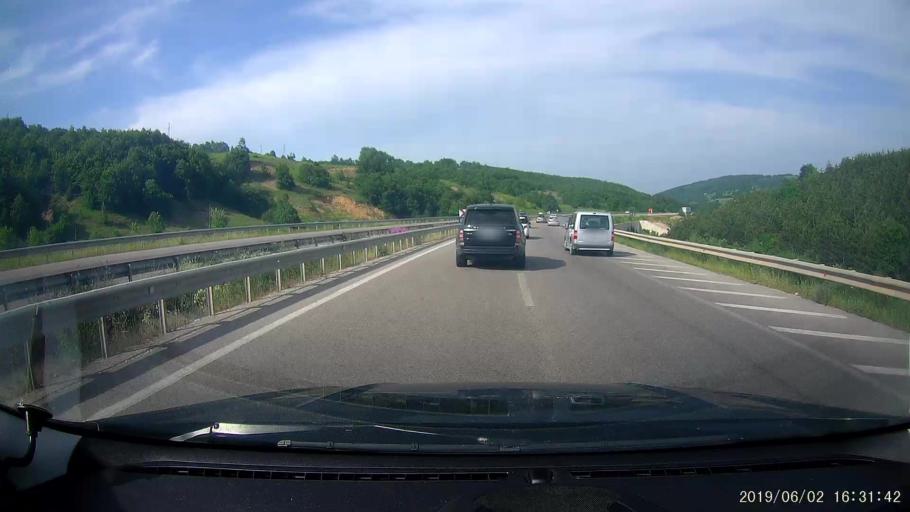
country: TR
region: Samsun
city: Ladik
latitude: 41.0348
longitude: 35.9050
